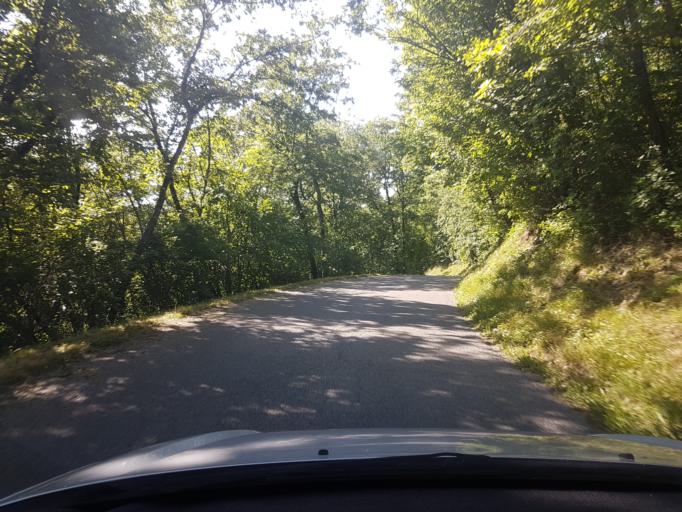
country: SI
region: Divaca
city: Divaca
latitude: 45.7477
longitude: 13.9984
